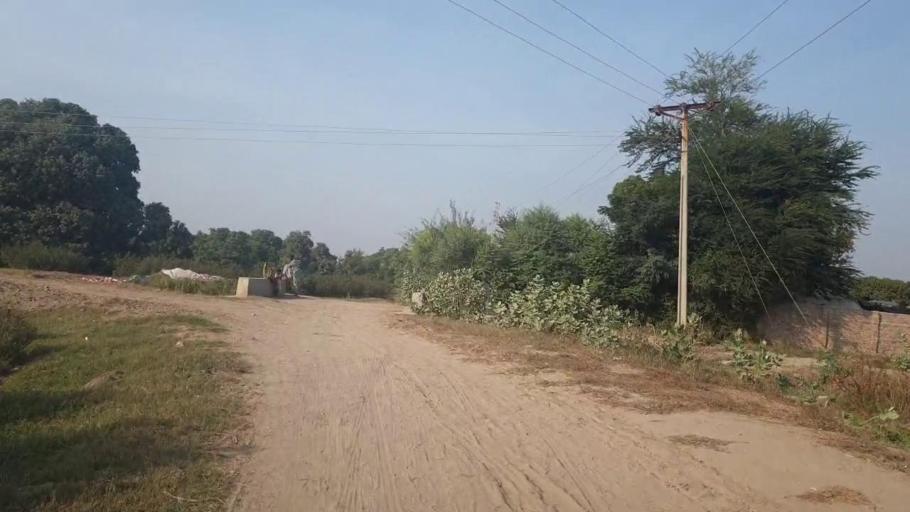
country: PK
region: Sindh
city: Tando Jam
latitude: 25.4278
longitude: 68.4649
